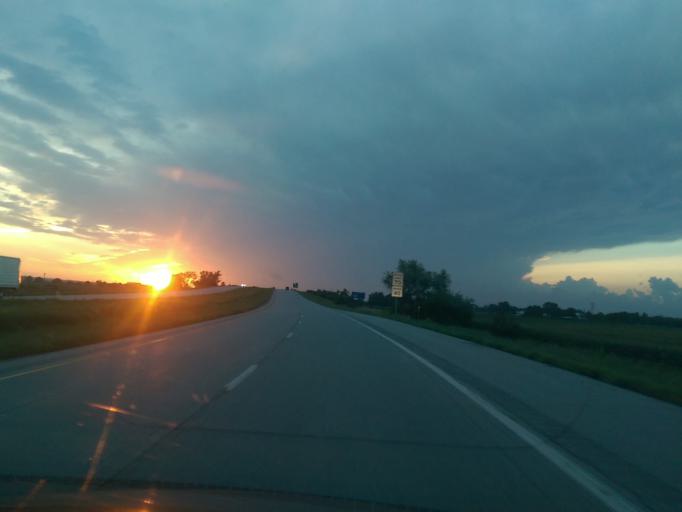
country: US
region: Iowa
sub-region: Fremont County
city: Hamburg
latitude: 40.5847
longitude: -95.6527
